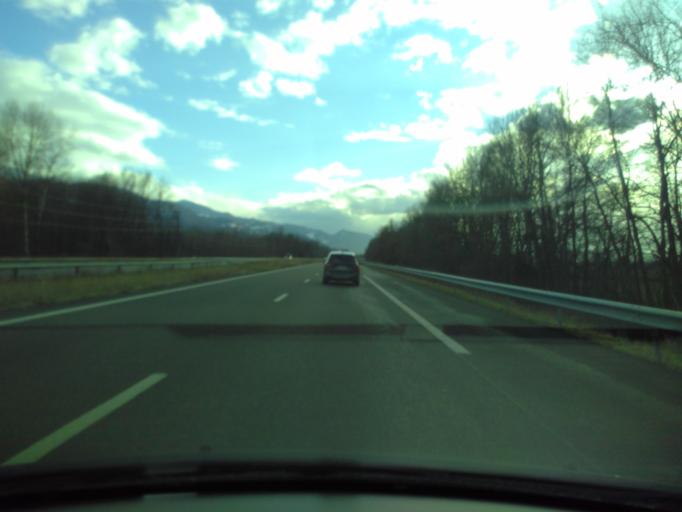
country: FR
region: Rhone-Alpes
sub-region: Departement de l'Isere
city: Lumbin
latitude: 45.2998
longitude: 5.9238
